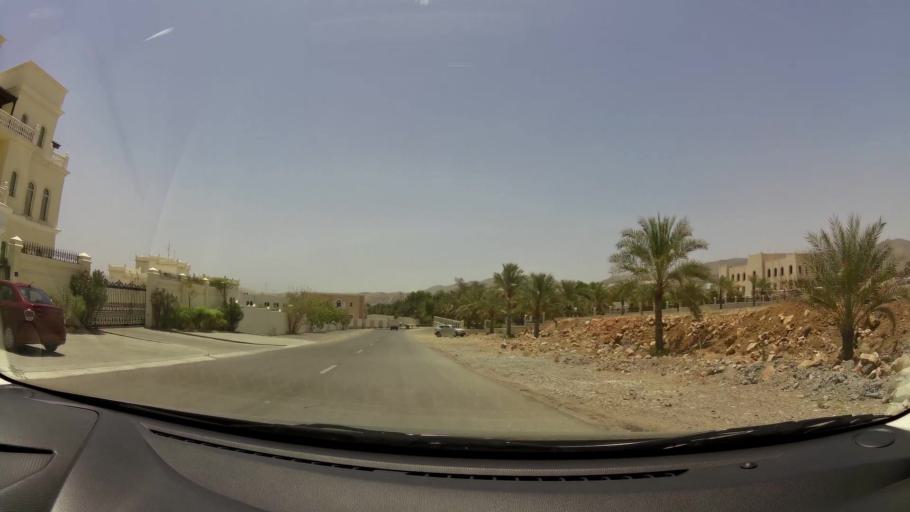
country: OM
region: Muhafazat Masqat
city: Bawshar
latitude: 23.6029
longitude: 58.4705
